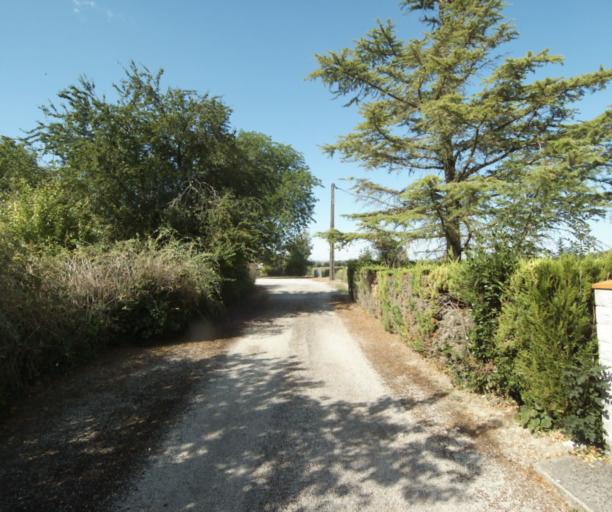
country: FR
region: Midi-Pyrenees
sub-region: Departement du Tarn
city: Puylaurens
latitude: 43.5205
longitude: 1.9856
